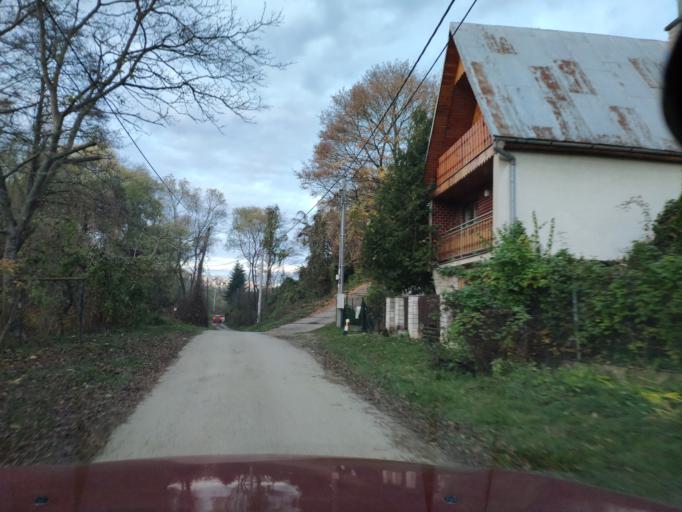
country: SK
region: Kosicky
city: Kosice
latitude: 48.6667
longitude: 21.3559
